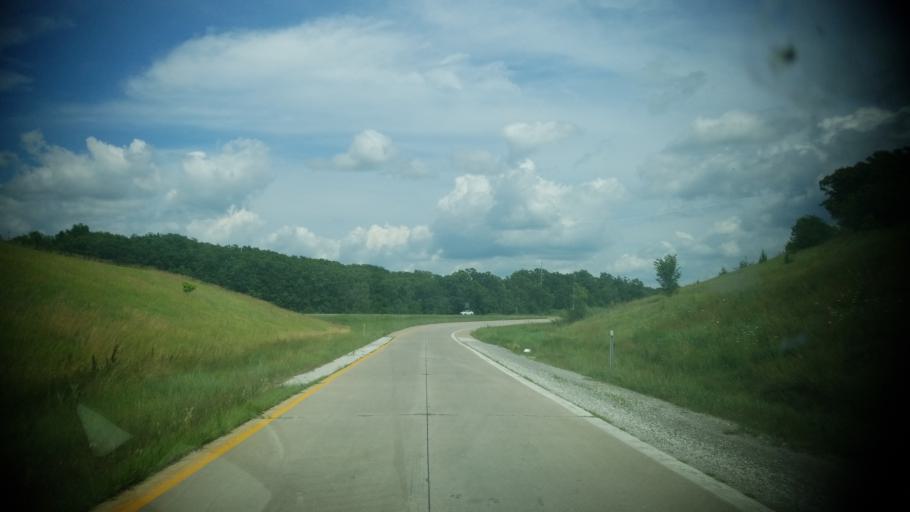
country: US
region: Missouri
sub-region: Pike County
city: Bowling Green
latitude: 39.3575
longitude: -91.2032
